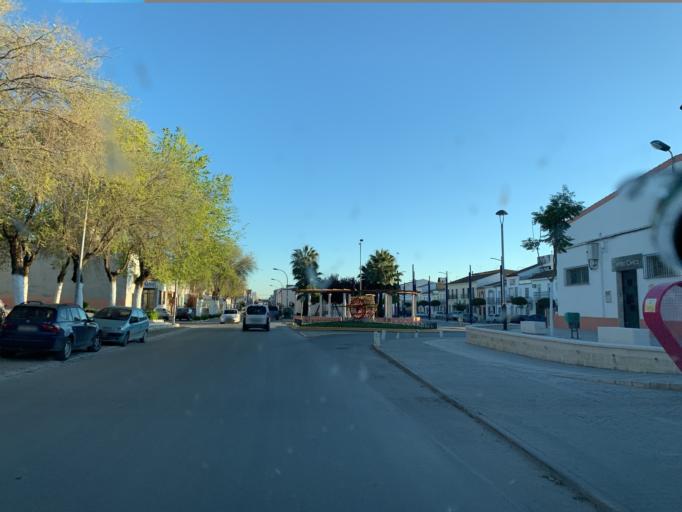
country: ES
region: Andalusia
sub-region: Provincia de Sevilla
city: Pedrera
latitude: 37.2281
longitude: -4.8933
